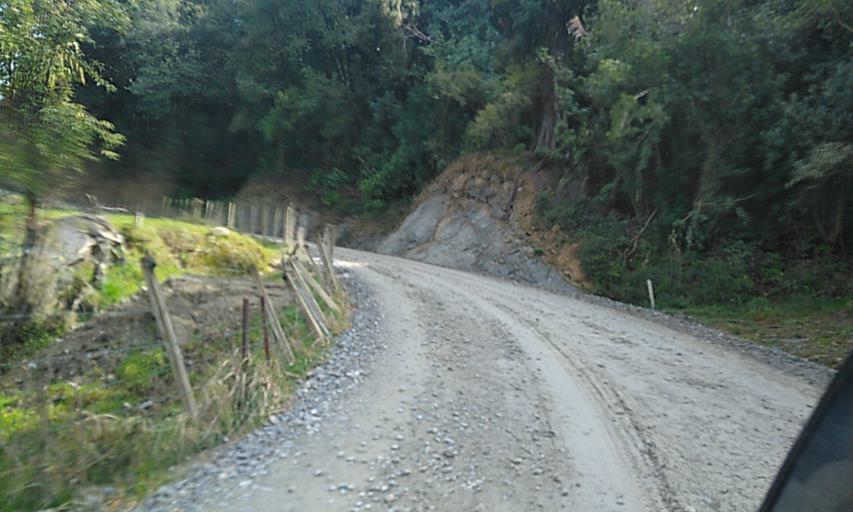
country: NZ
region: Gisborne
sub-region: Gisborne District
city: Gisborne
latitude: -38.3160
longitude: 178.0856
